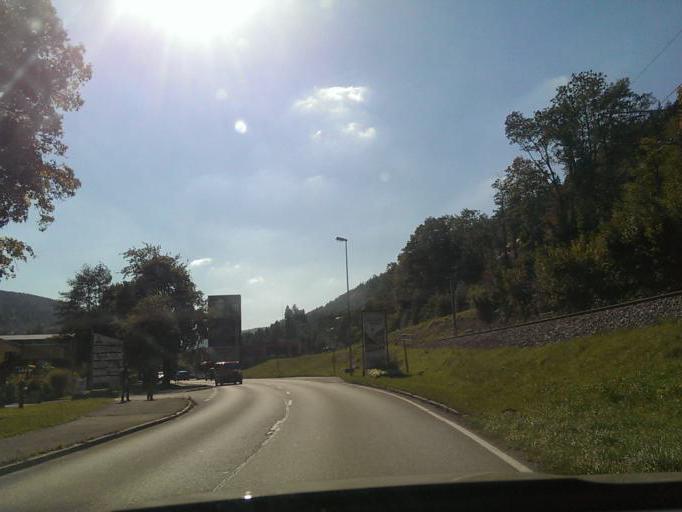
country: DE
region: Baden-Wuerttemberg
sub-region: Karlsruhe Region
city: Bad Wildbad
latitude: 48.7618
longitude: 8.5525
